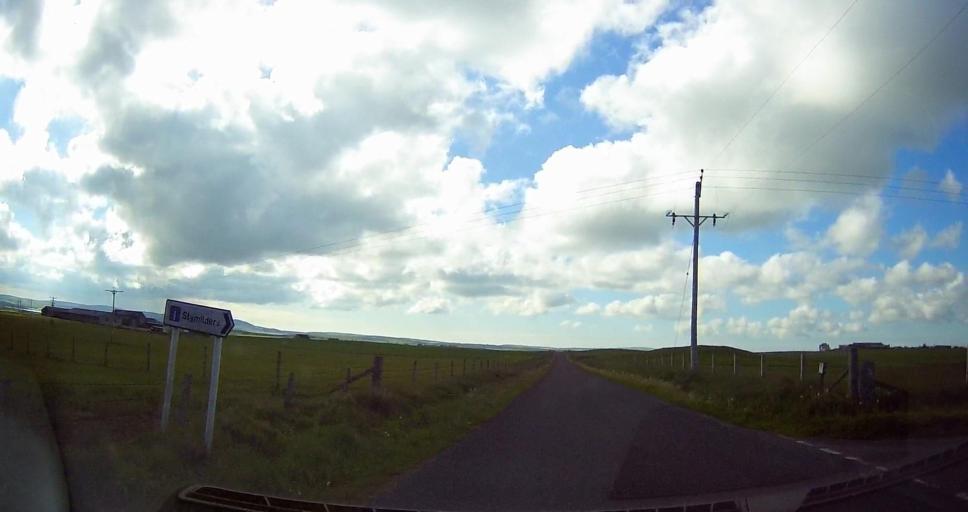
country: GB
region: Scotland
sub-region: Orkney Islands
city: Stromness
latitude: 58.9964
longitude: -3.1632
